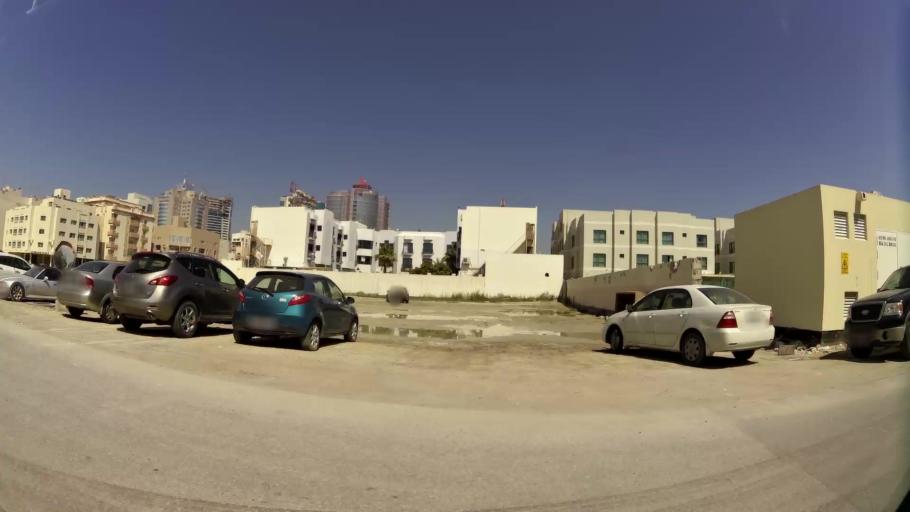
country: BH
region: Manama
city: Manama
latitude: 26.2111
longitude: 50.6133
